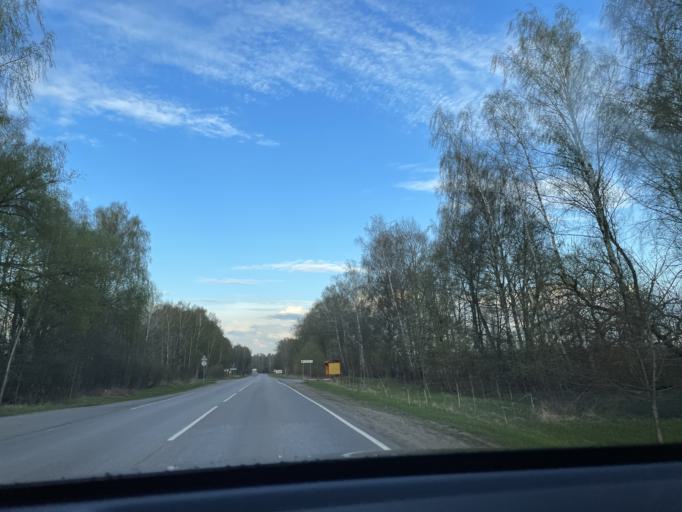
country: RU
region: Tula
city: Novogurovskiy
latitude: 54.5193
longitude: 37.2347
